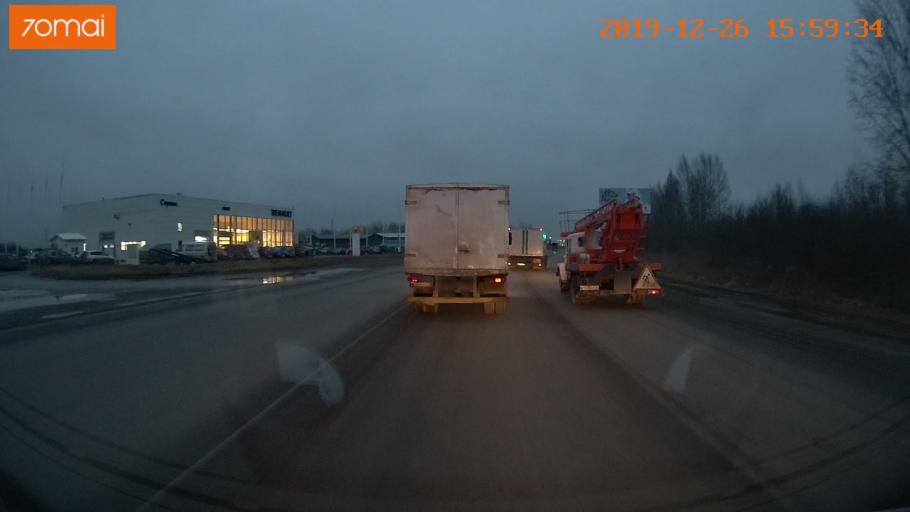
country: RU
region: Jaroslavl
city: Rybinsk
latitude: 58.0306
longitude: 38.8046
